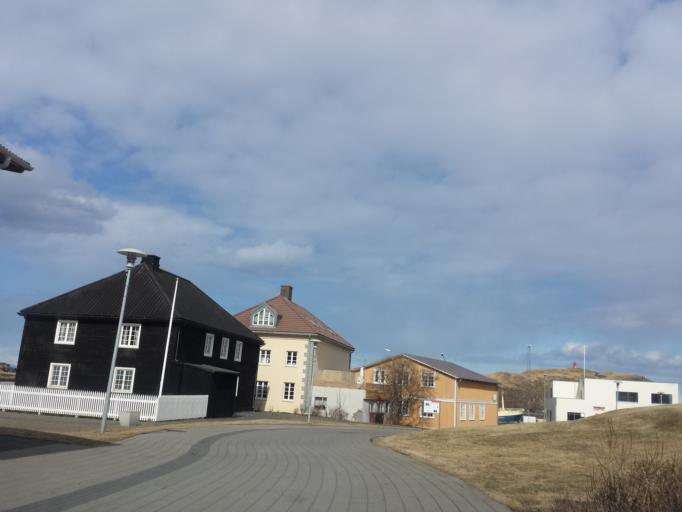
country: IS
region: West
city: Stykkisholmur
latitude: 65.0768
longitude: -22.7266
